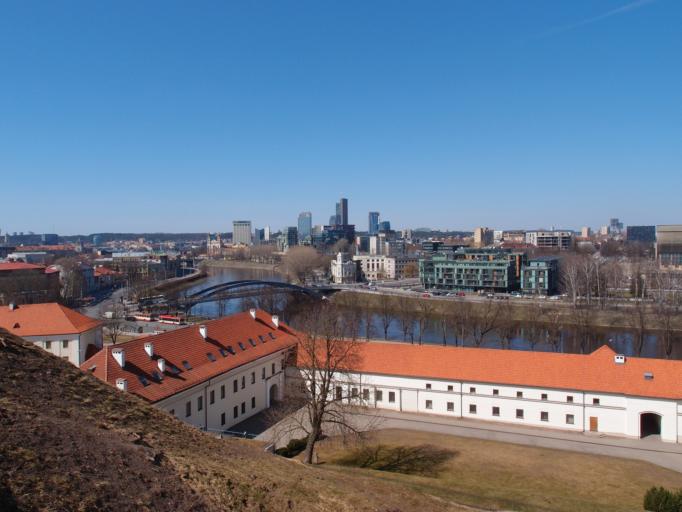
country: LT
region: Vilnius County
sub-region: Vilnius
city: Vilnius
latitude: 54.6872
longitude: 25.2918
